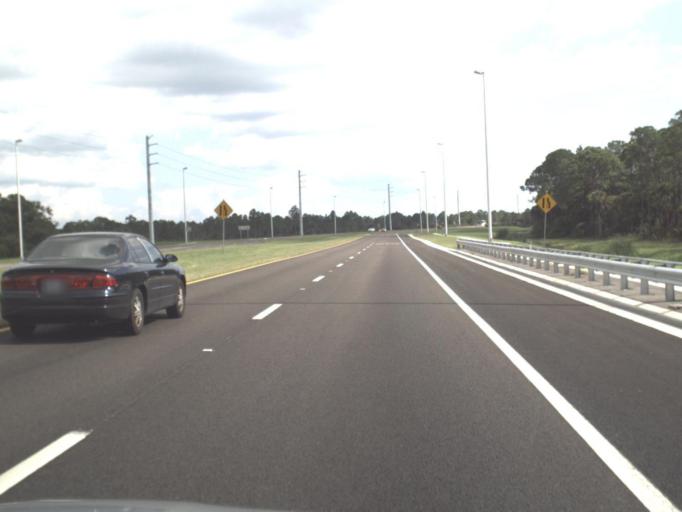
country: US
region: Florida
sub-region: Sarasota County
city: Warm Mineral Springs
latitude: 27.0407
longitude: -82.2995
